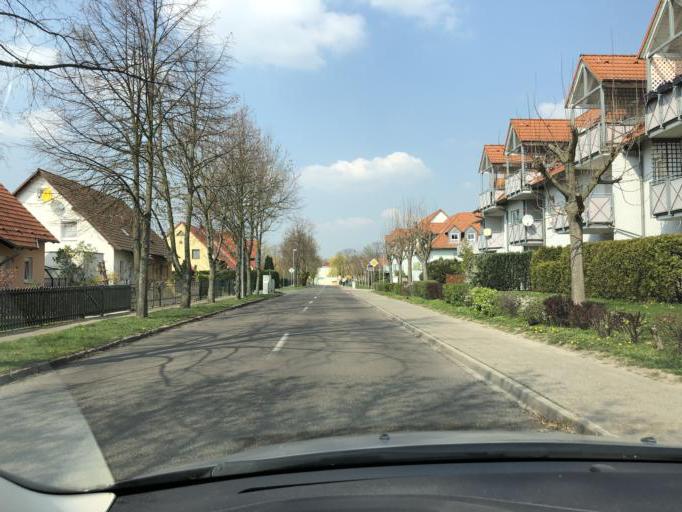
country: DE
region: Saxony-Anhalt
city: Landsberg
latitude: 51.5303
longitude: 12.1503
